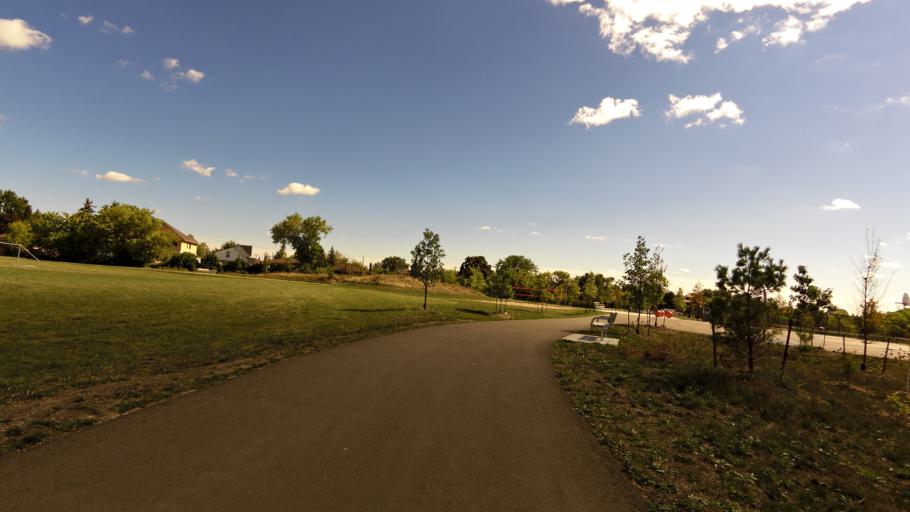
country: CA
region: Ontario
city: Etobicoke
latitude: 43.7070
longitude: -79.6505
